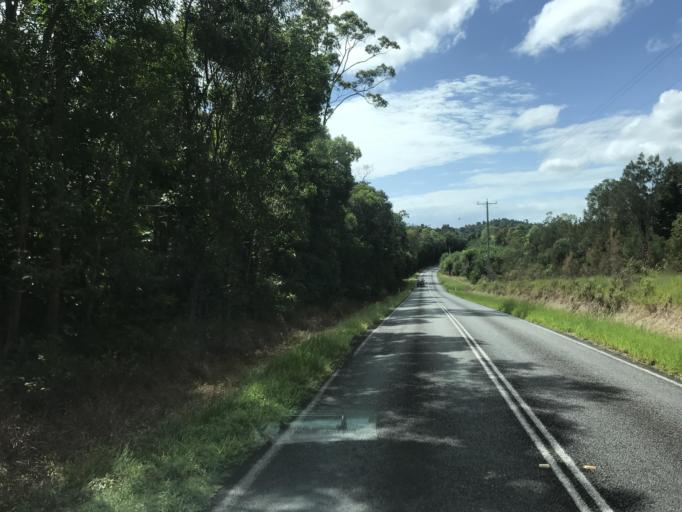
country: AU
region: Queensland
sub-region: Cassowary Coast
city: Innisfail
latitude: -17.8432
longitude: 146.0555
